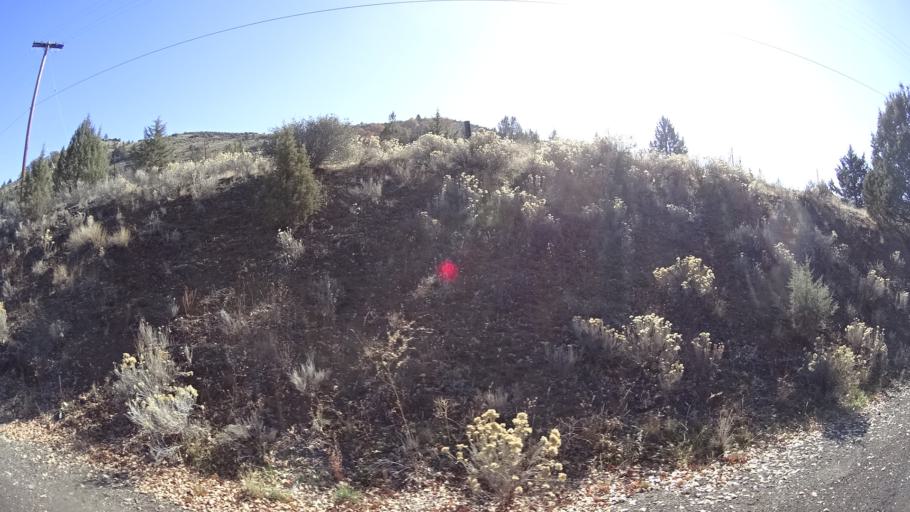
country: US
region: California
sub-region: Siskiyou County
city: Yreka
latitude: 41.7719
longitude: -122.6032
